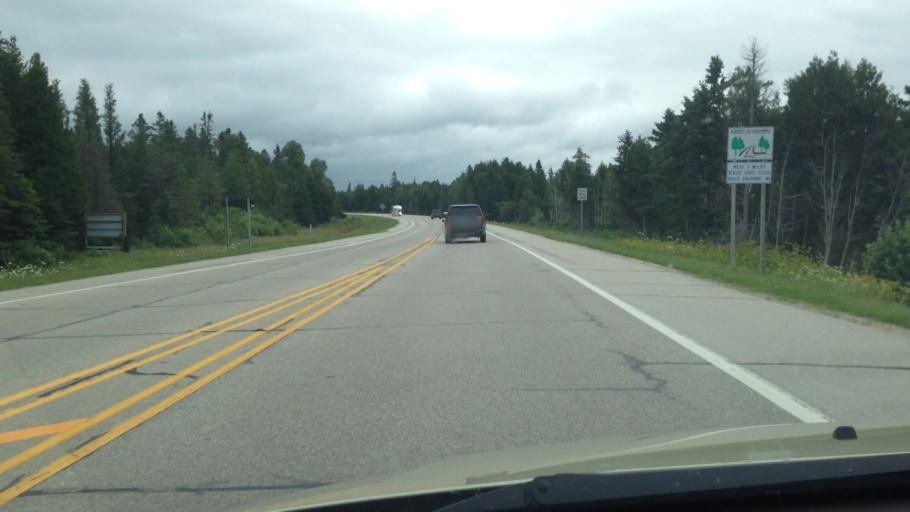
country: US
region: Michigan
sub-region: Luce County
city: Newberry
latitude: 46.0961
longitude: -85.4420
